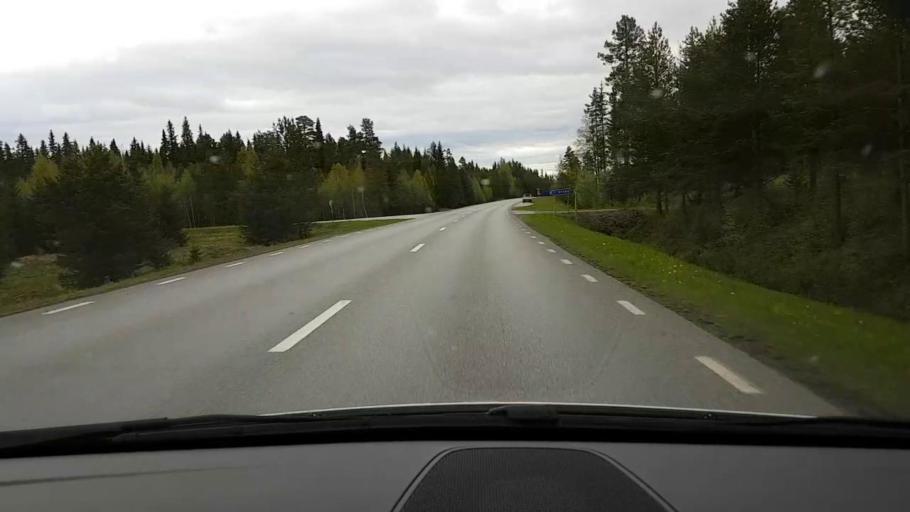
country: SE
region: Jaemtland
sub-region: Krokoms Kommun
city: Valla
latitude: 63.3050
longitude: 13.9237
